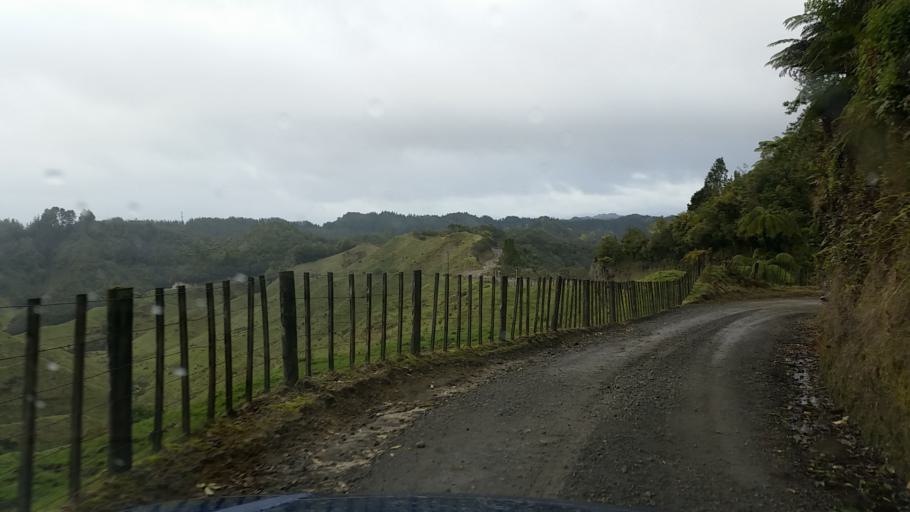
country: NZ
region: Taranaki
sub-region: South Taranaki District
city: Eltham
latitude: -39.1702
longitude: 174.6261
